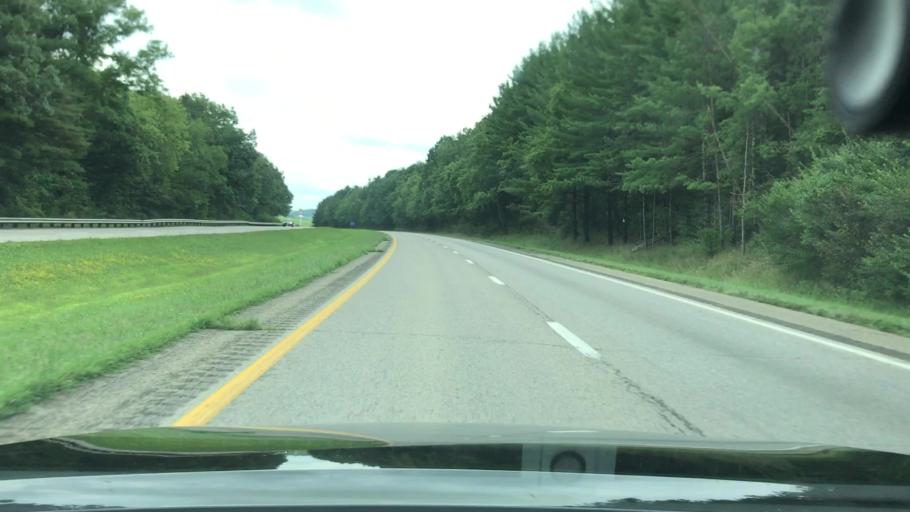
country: US
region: Ohio
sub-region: Jackson County
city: Jackson
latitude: 39.0024
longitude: -82.5619
